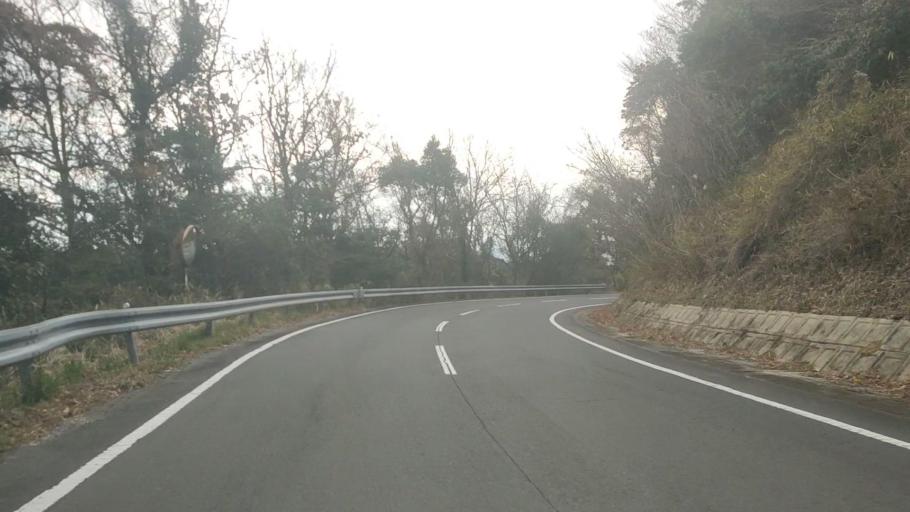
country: JP
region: Nagasaki
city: Shimabara
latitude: 32.7171
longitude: 130.2467
